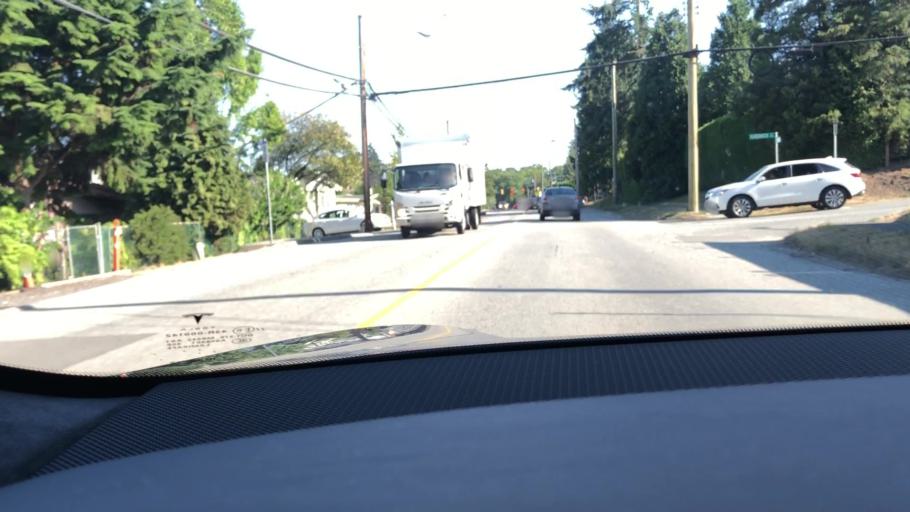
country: CA
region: British Columbia
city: Burnaby
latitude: 49.2519
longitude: -122.9817
